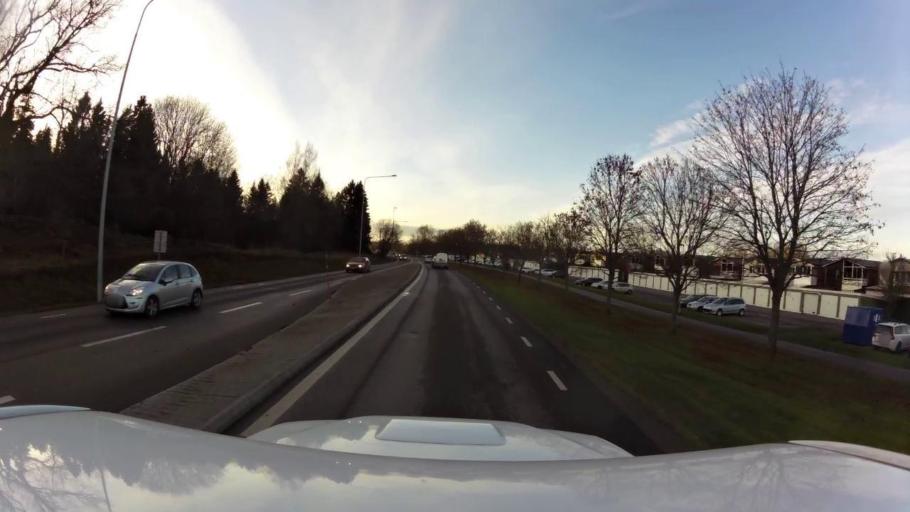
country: SE
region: OEstergoetland
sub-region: Linkopings Kommun
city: Linkoping
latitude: 58.3732
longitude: 15.6756
